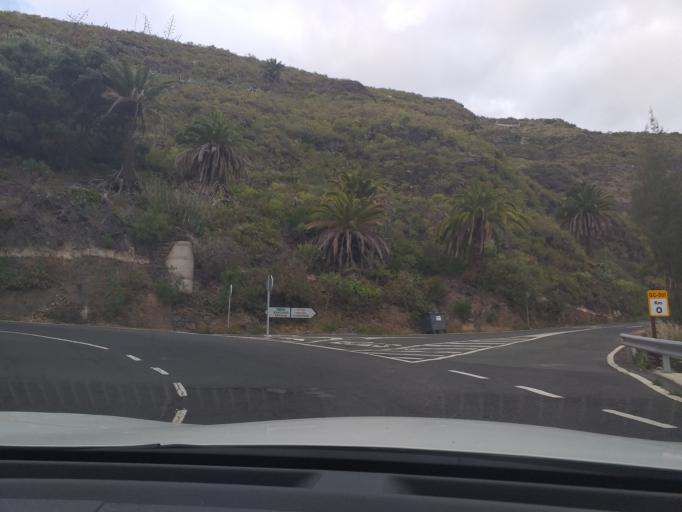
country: ES
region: Canary Islands
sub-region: Provincia de Las Palmas
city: Arucas
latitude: 28.1102
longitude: -15.5004
